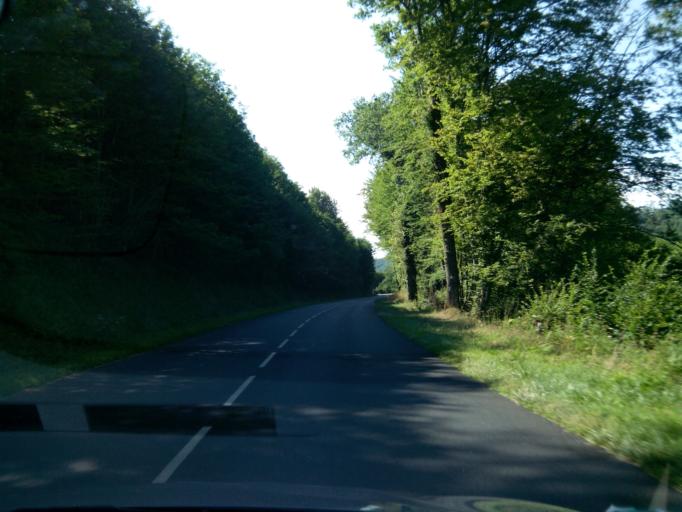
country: FR
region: Limousin
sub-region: Departement de la Correze
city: Beynat
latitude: 45.1216
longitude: 1.6994
